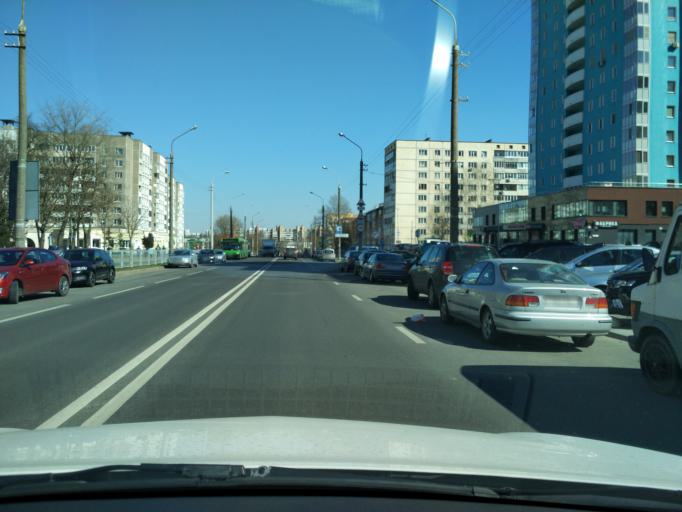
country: BY
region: Minsk
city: Minsk
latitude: 53.8775
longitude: 27.5542
